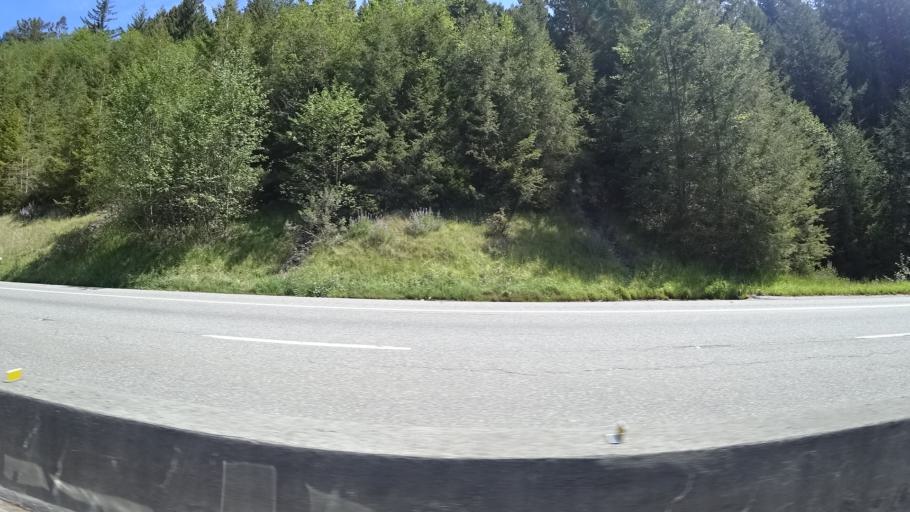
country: US
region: California
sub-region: Humboldt County
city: Westhaven-Moonstone
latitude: 41.3729
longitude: -123.9916
